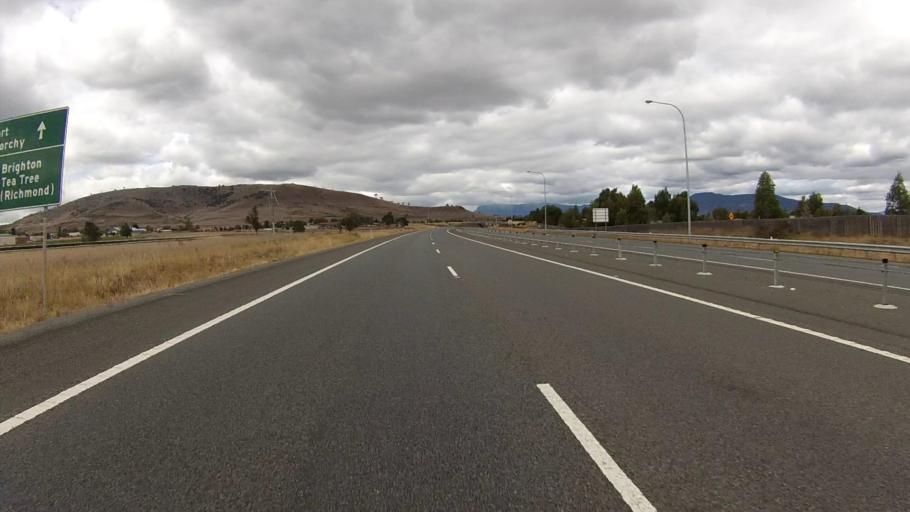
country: AU
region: Tasmania
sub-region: Brighton
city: Bridgewater
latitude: -42.6896
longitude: 147.2785
